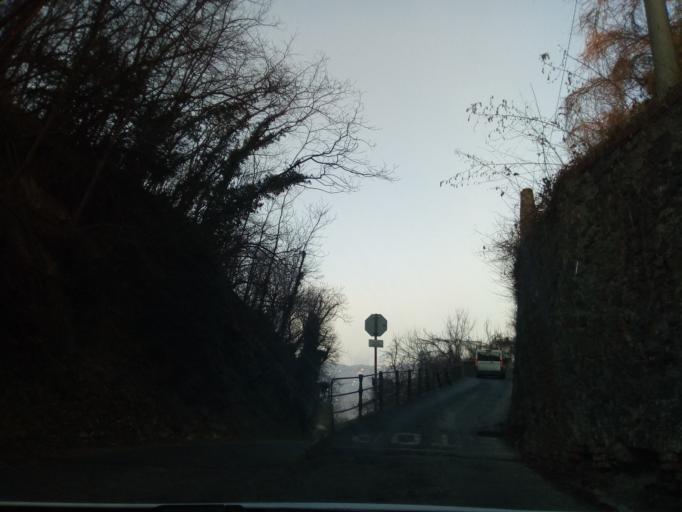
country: IT
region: Piedmont
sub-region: Provincia di Torino
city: Salerano Canavese
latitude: 45.4573
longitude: 7.8482
